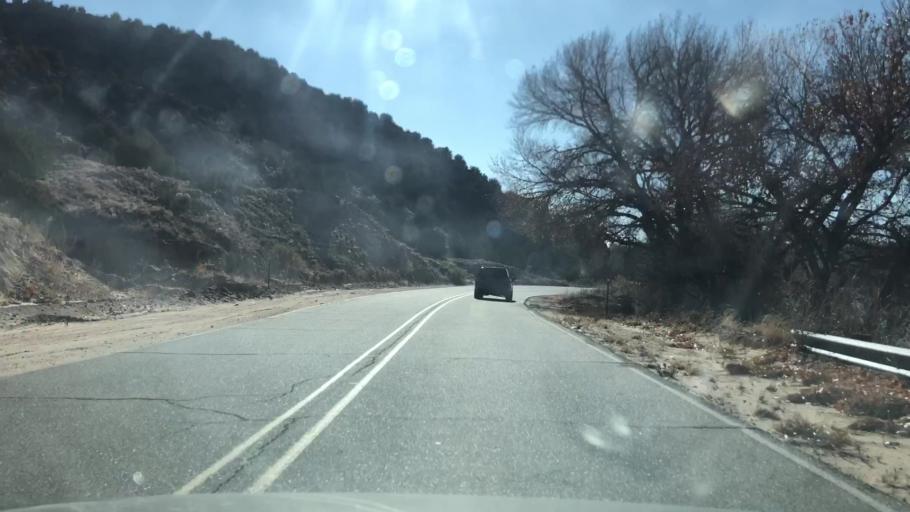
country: US
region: New Mexico
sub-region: Rio Arriba County
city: Ohkay Owingeh
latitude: 36.0916
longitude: -106.1295
